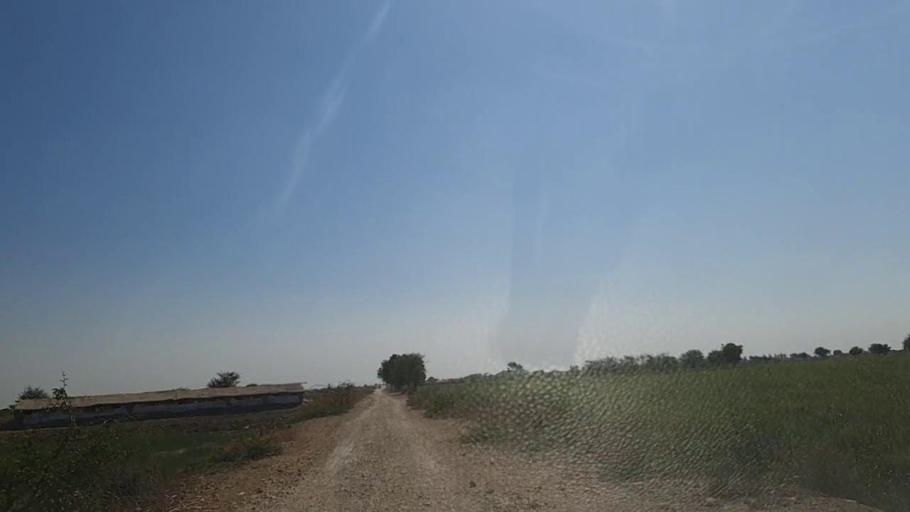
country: PK
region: Sindh
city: Kunri
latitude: 25.2782
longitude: 69.5226
